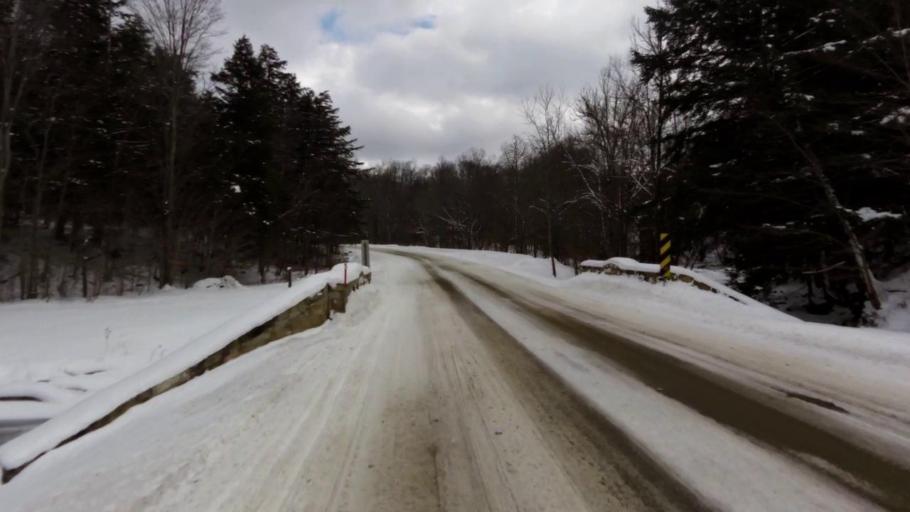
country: US
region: Pennsylvania
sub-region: McKean County
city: Bradford
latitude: 42.0095
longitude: -78.8016
